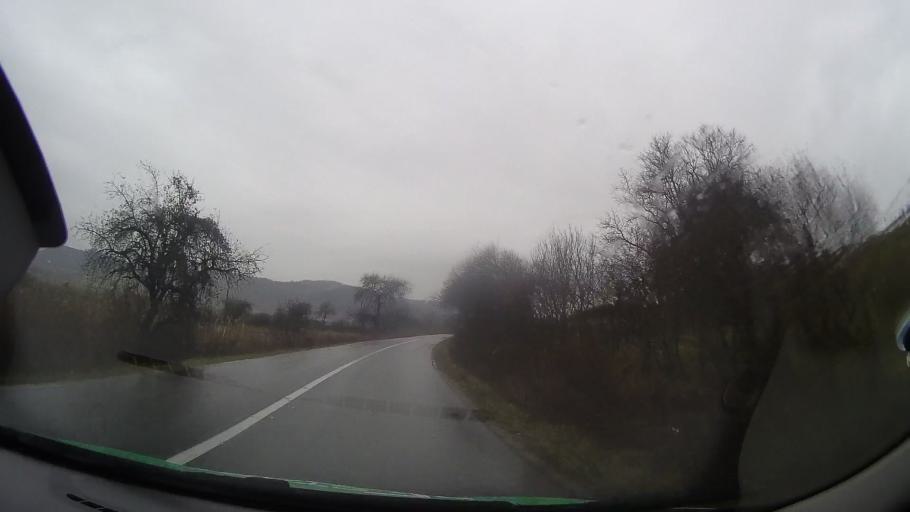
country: RO
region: Bistrita-Nasaud
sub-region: Comuna Mariselu
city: Mariselu
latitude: 47.0159
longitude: 24.5327
